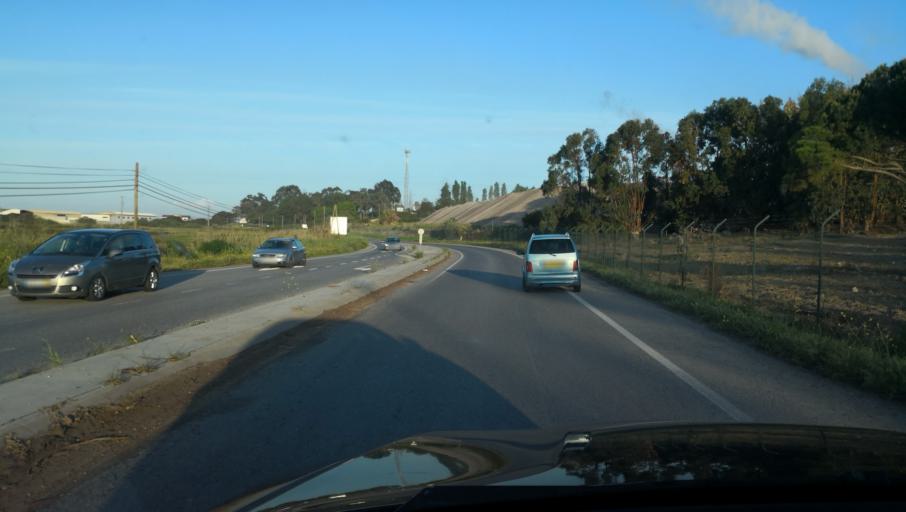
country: PT
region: Setubal
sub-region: Setubal
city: Setubal
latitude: 38.4904
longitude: -8.8008
